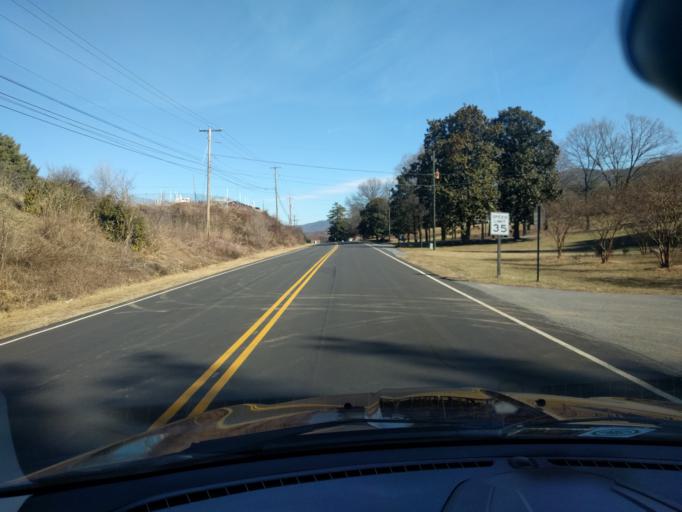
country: US
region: Virginia
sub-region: Roanoke County
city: Vinton
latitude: 37.3172
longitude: -79.8772
